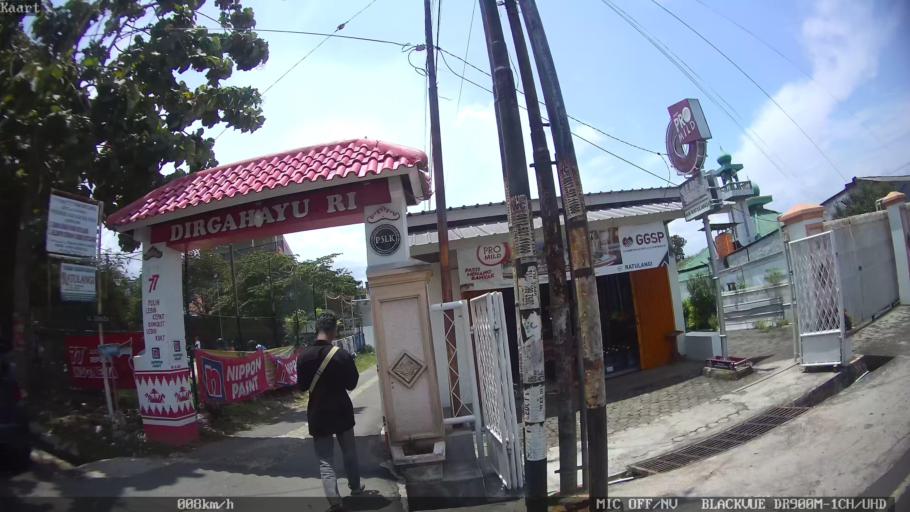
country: ID
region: Lampung
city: Kedaton
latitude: -5.4006
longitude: 105.2542
